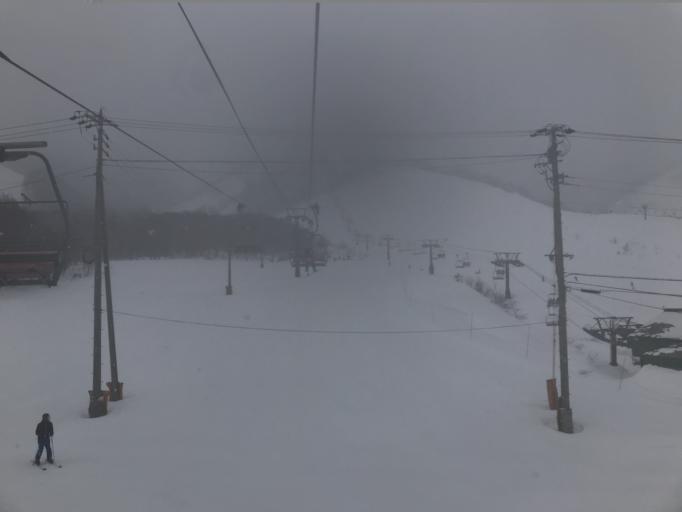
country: JP
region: Nagano
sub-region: Kitaazumi Gun
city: Hakuba
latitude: 36.7560
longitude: 137.8631
